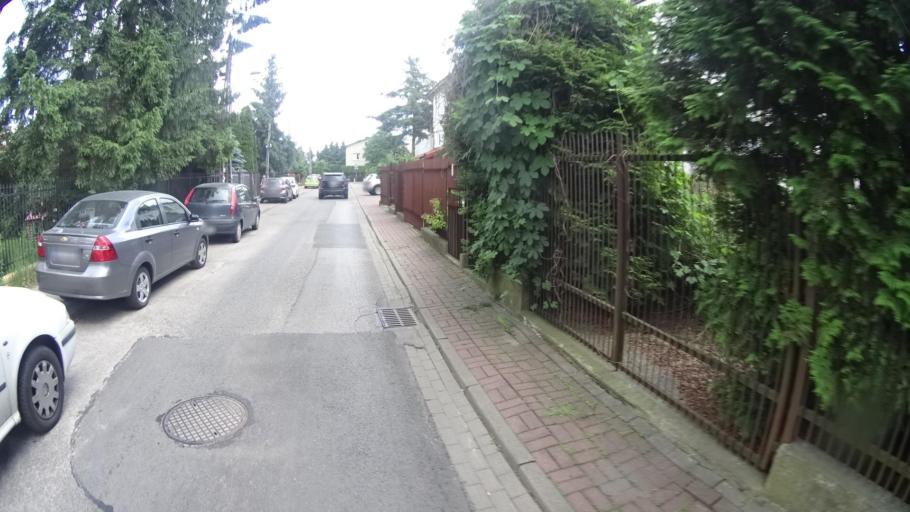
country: PL
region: Masovian Voivodeship
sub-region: Warszawa
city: Wlochy
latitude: 52.2038
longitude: 20.9290
